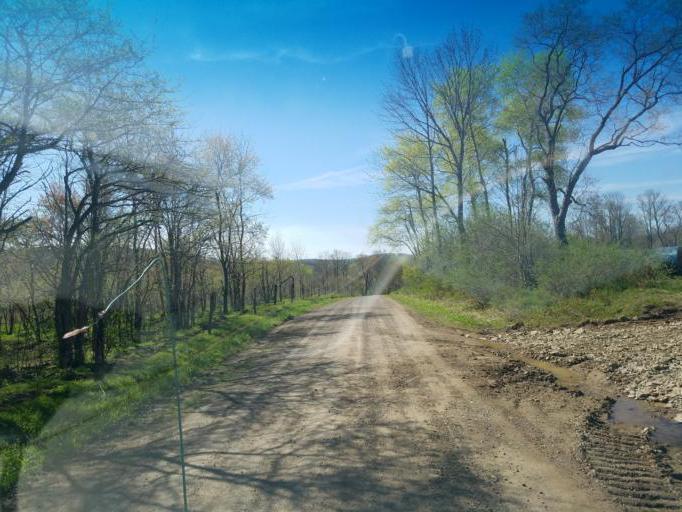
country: US
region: New York
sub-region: Allegany County
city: Andover
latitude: 41.9689
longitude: -77.7838
